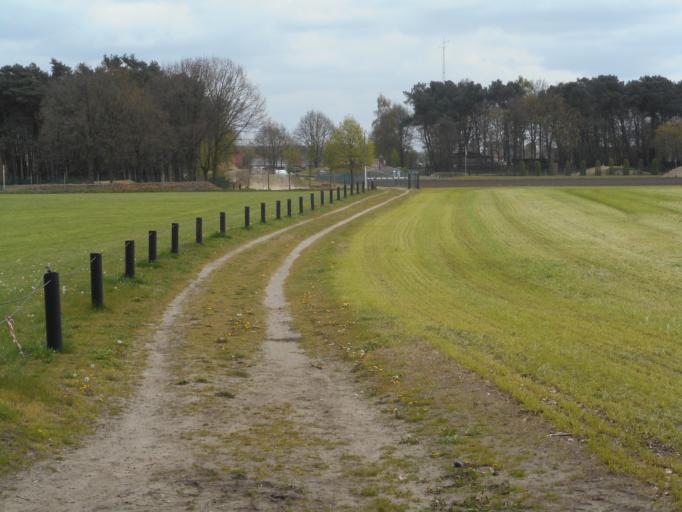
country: BE
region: Flanders
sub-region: Provincie Antwerpen
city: Wuustwezel
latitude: 51.3953
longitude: 4.5726
